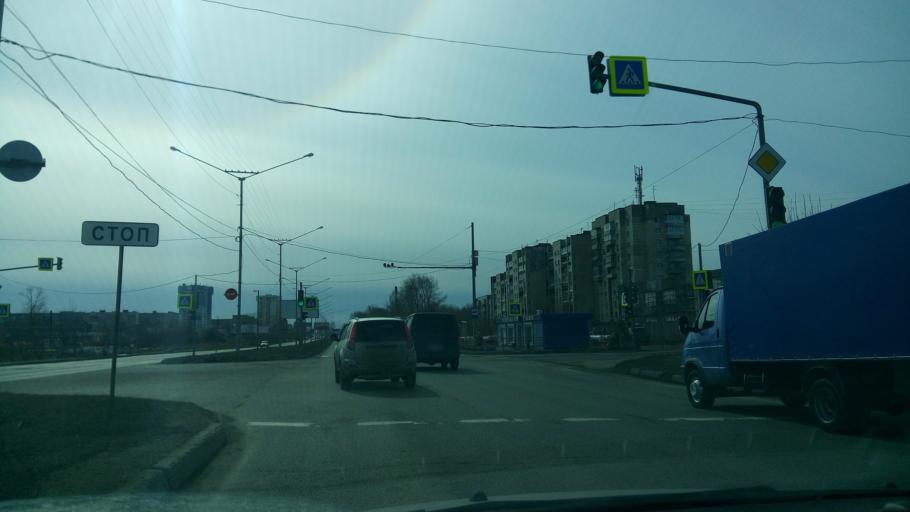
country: RU
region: Sverdlovsk
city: Nizhniy Tagil
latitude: 57.8903
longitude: 59.9407
